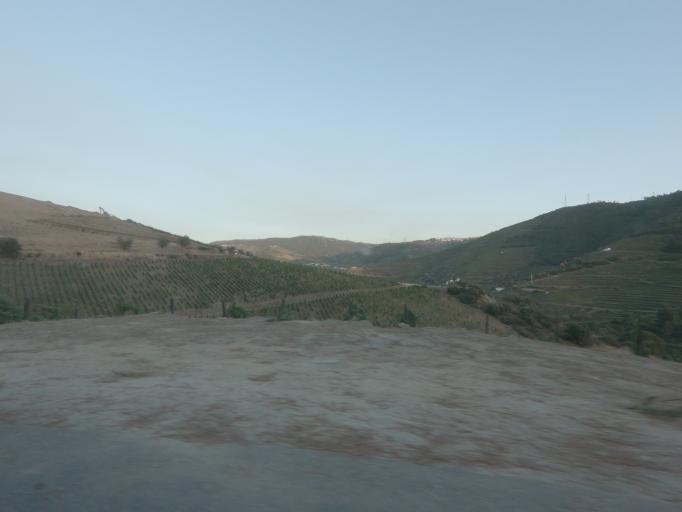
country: PT
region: Viseu
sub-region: Armamar
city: Armamar
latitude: 41.1461
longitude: -7.7034
